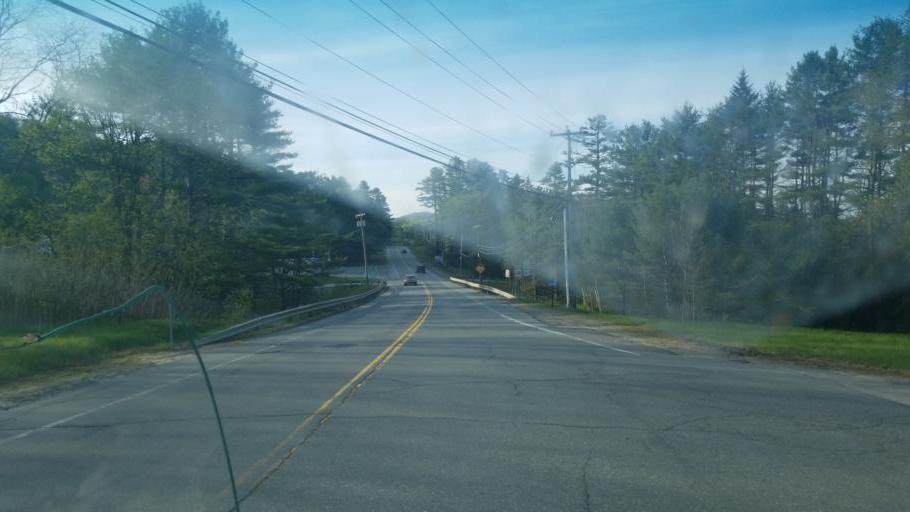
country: US
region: New Hampshire
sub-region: Grafton County
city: Littleton
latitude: 44.3162
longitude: -71.7969
